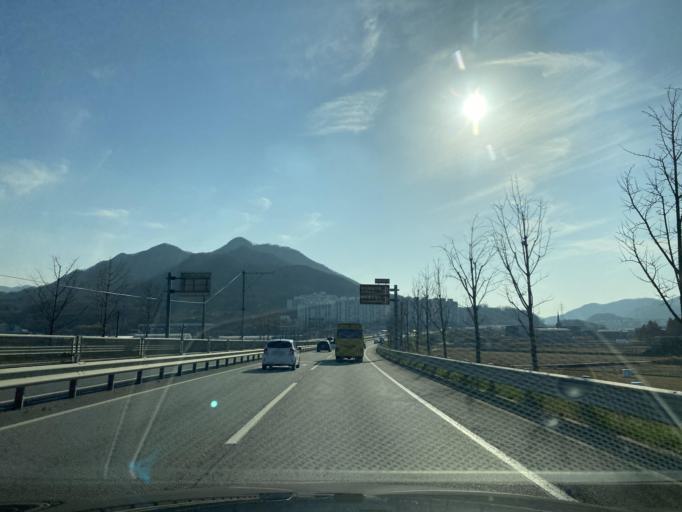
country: KR
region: Chungcheongnam-do
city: Asan
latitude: 36.7605
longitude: 127.0352
